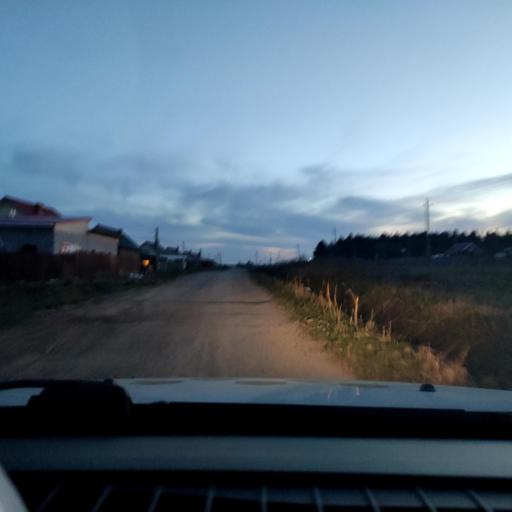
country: RU
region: Perm
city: Ferma
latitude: 57.9402
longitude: 56.3377
